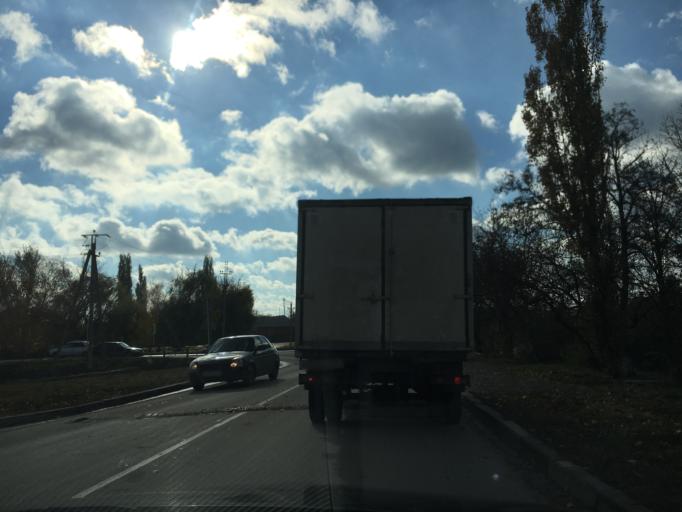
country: RU
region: Rostov
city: Matveyev Kurgan
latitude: 47.5639
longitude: 38.8735
